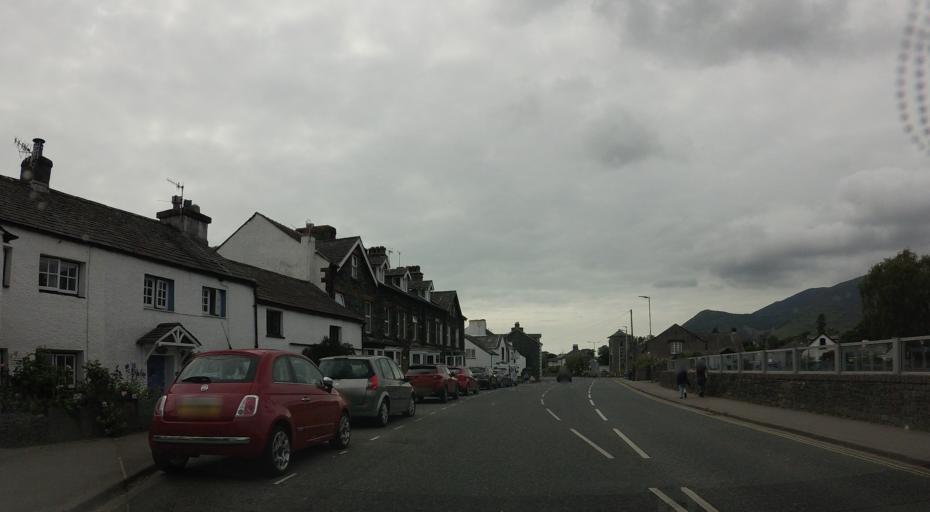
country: GB
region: England
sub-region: Cumbria
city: Keswick
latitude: 54.6043
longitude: -3.1441
